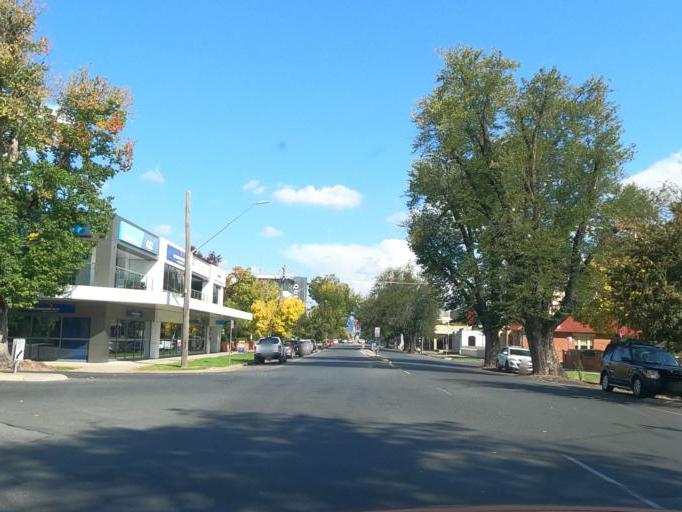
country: AU
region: New South Wales
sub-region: Albury Municipality
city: Albury
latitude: -36.0764
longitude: 146.9165
